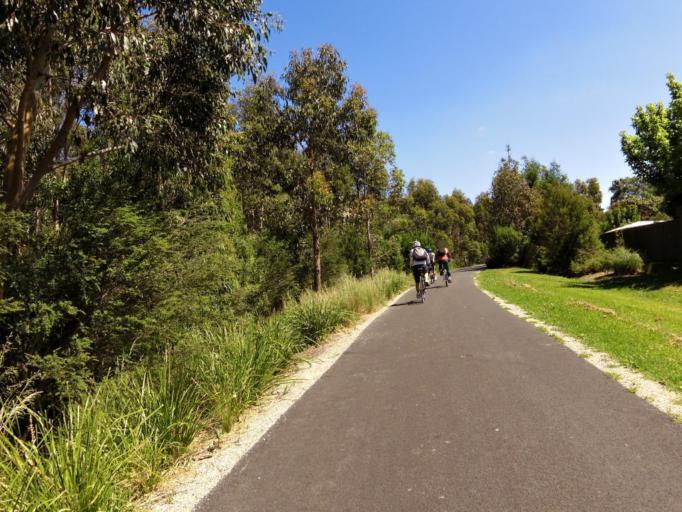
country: AU
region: Victoria
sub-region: Knox
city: Knoxfield
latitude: -37.8990
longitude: 145.2678
